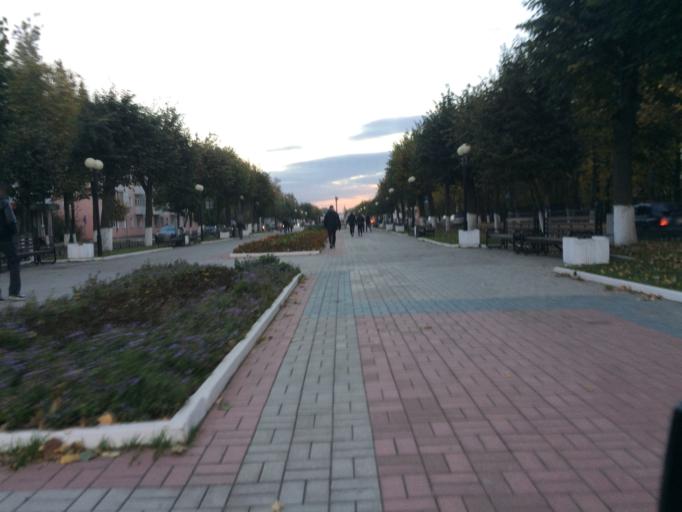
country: RU
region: Mariy-El
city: Yoshkar-Ola
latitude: 56.6390
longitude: 47.8777
